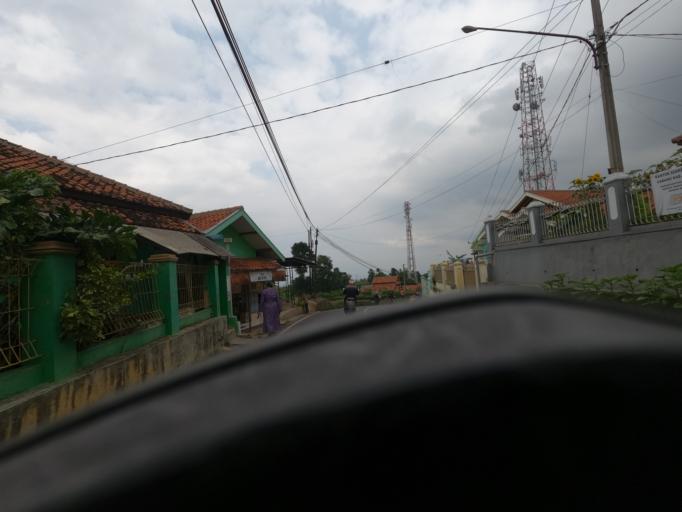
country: ID
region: West Java
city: Cimahi
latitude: -6.8212
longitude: 107.5362
